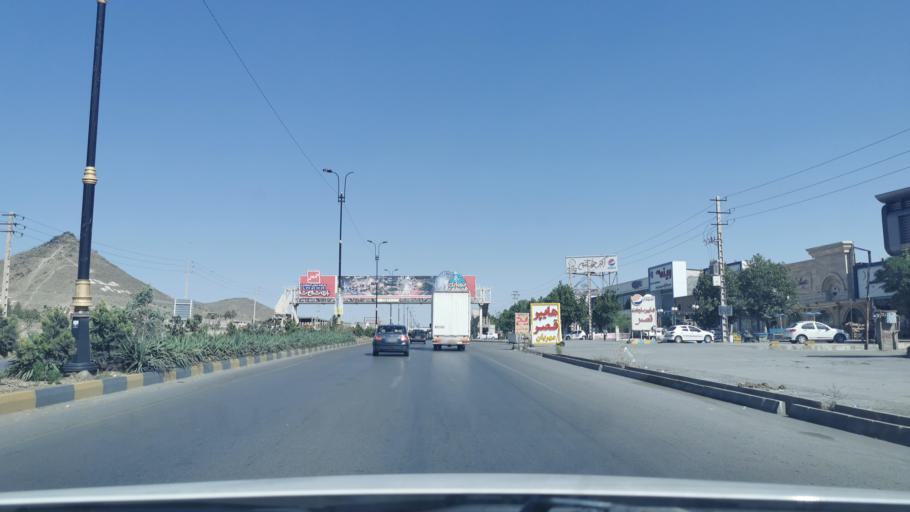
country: IR
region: Razavi Khorasan
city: Torqabeh
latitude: 36.3926
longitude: 59.4021
